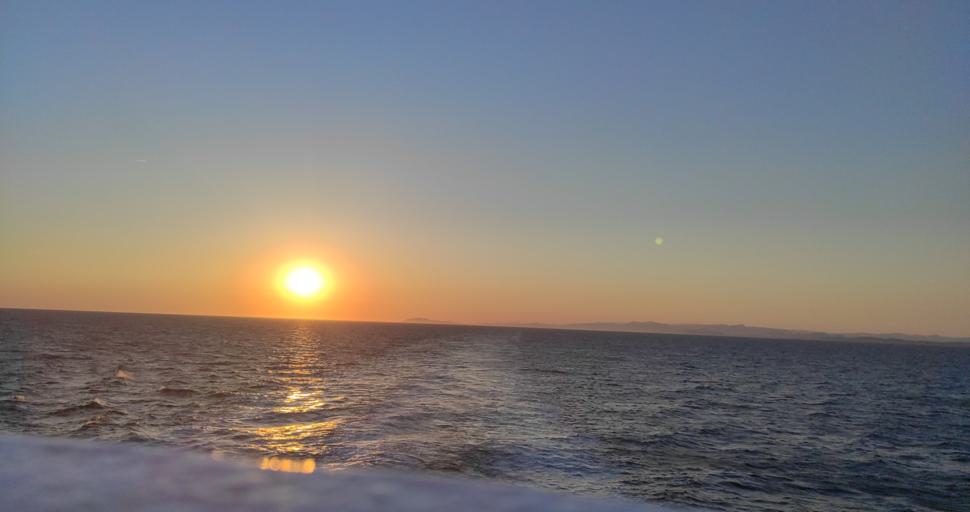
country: FR
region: Provence-Alpes-Cote d'Azur
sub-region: Departement du Var
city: La Londe-les-Maures
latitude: 42.8487
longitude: 6.2750
